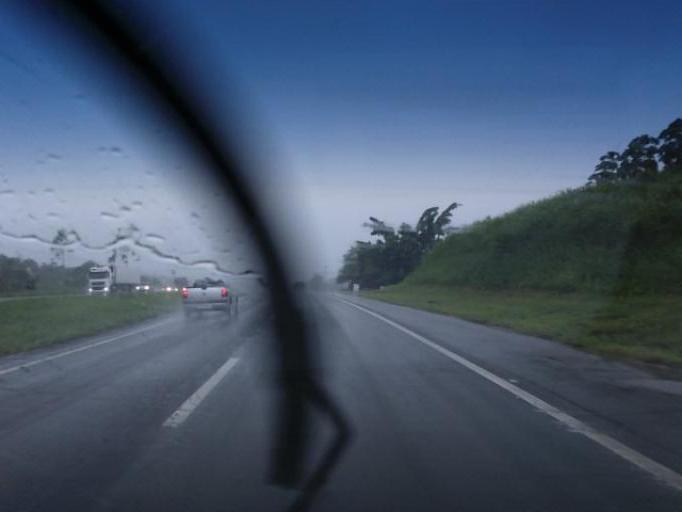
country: BR
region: Sao Paulo
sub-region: Miracatu
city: Miracatu
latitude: -24.2794
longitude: -47.4223
